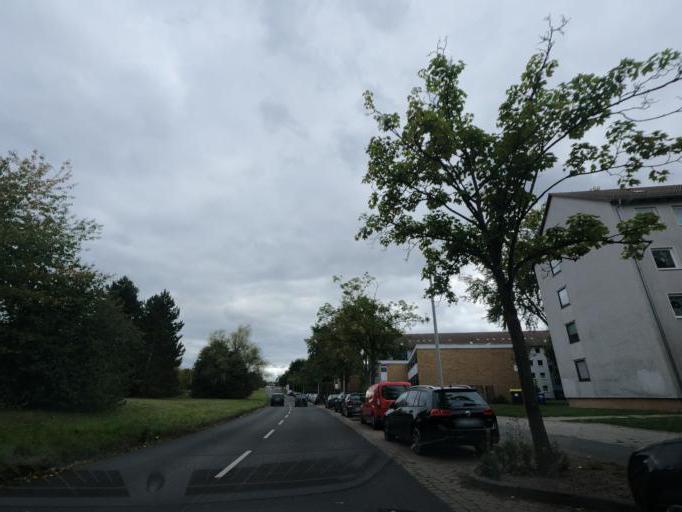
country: DE
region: Lower Saxony
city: Leiferde
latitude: 52.2405
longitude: 10.4875
